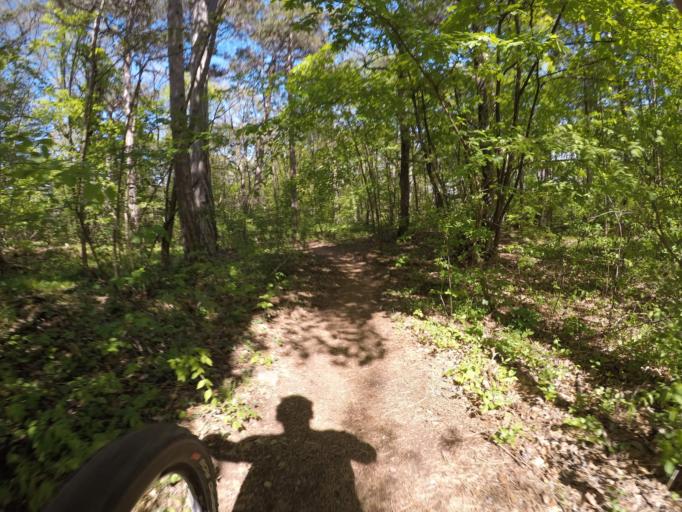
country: AT
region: Lower Austria
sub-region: Politischer Bezirk Modling
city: Gumpoldskirchen
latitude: 48.0650
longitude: 16.2812
